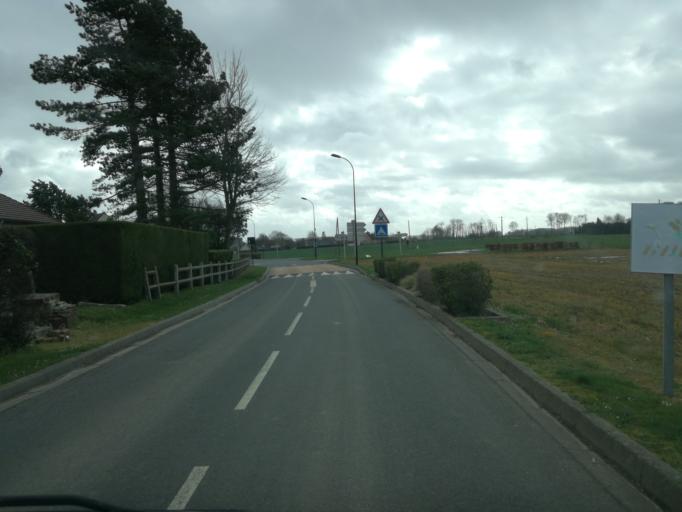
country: FR
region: Haute-Normandie
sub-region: Departement de la Seine-Maritime
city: Yebleron
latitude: 49.6676
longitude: 0.4980
